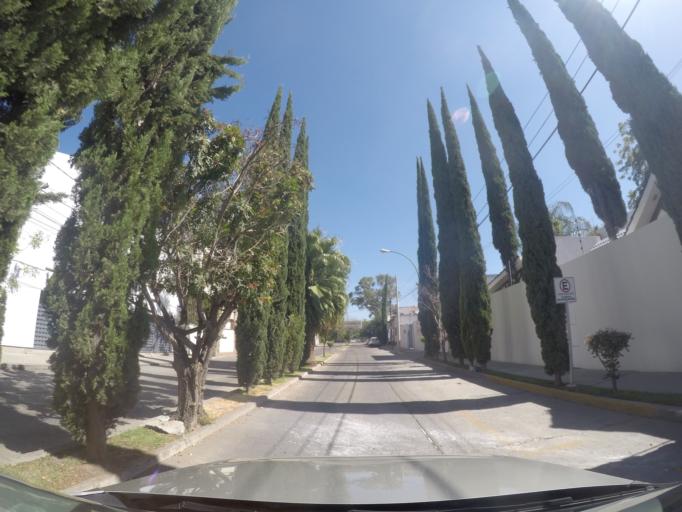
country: MX
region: San Luis Potosi
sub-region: San Luis Potosi
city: San Luis Potosi
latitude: 22.1497
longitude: -101.0122
